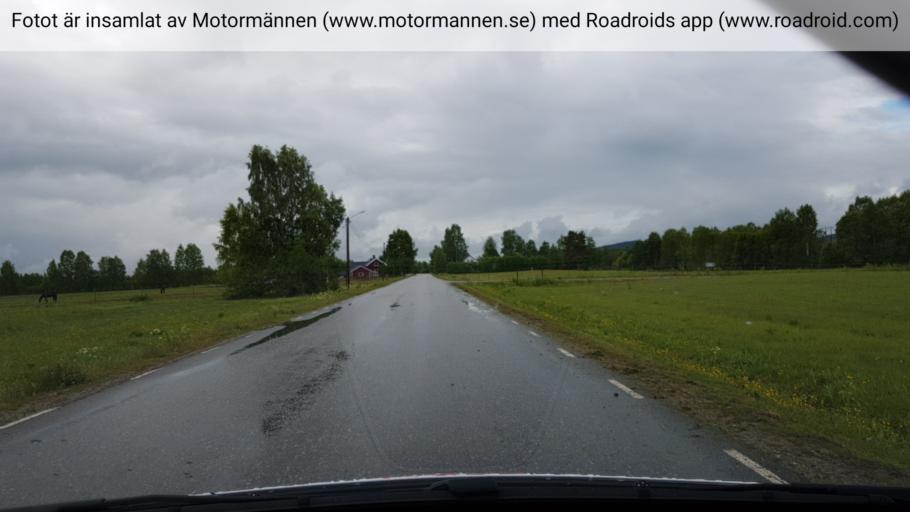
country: SE
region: Vaesterbotten
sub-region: Vannas Kommun
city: Vannasby
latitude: 63.9296
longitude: 19.8551
